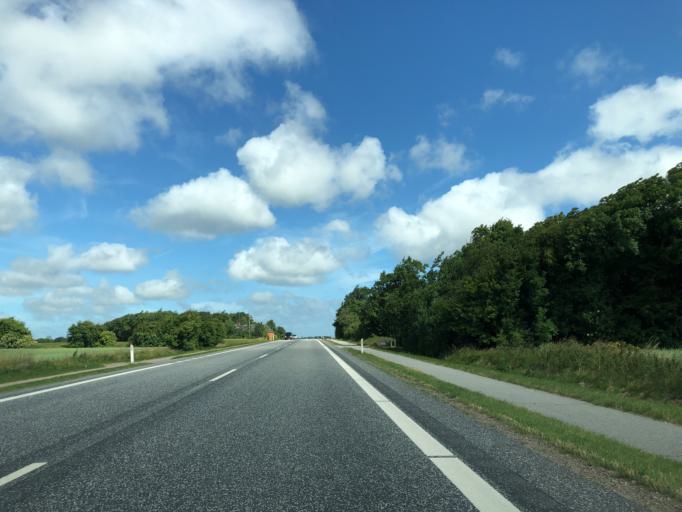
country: DK
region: Central Jutland
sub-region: Struer Kommune
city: Struer
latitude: 56.4425
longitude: 8.5949
